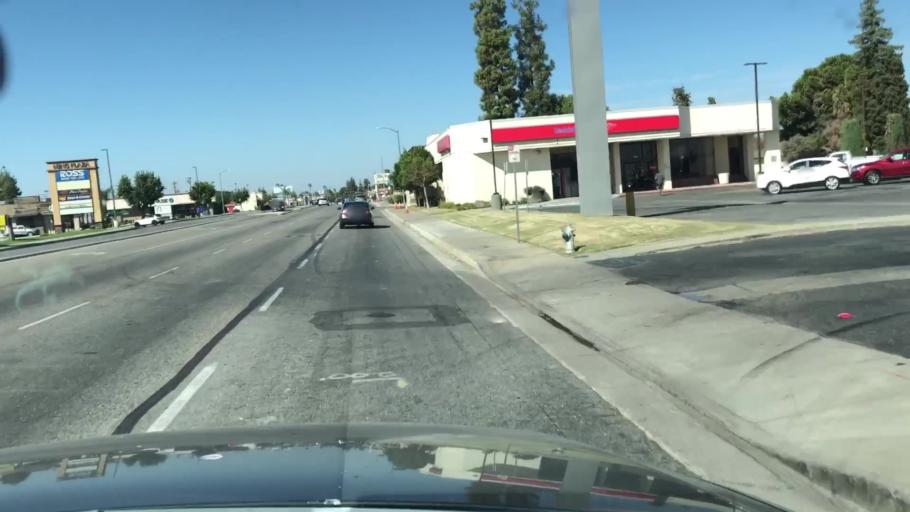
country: US
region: California
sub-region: Kern County
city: Bakersfield
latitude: 35.3396
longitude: -119.0452
